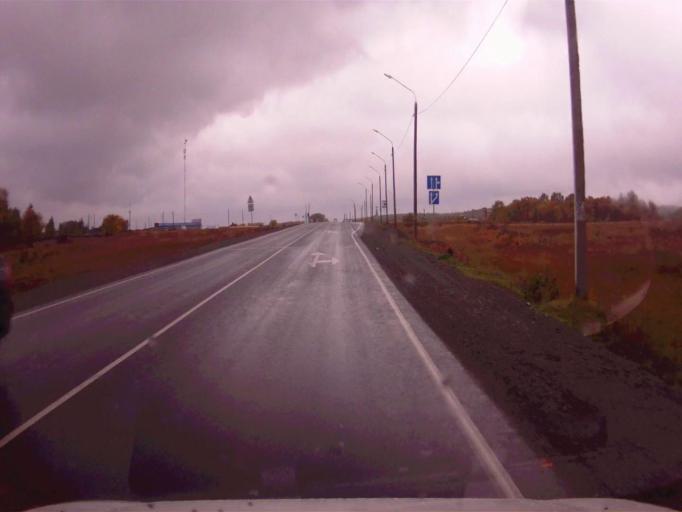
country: RU
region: Chelyabinsk
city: Tayginka
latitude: 55.4975
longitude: 60.6425
